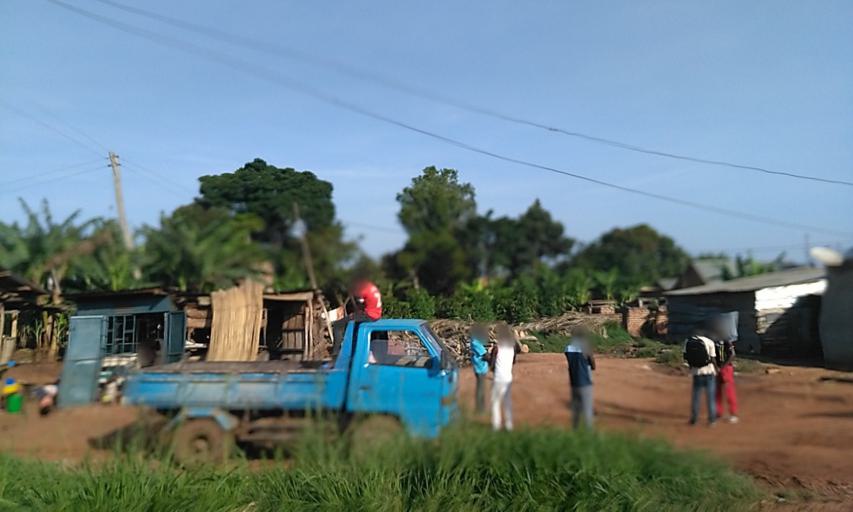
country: UG
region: Central Region
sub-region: Wakiso District
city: Bweyogerere
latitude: 0.4724
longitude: 32.6620
